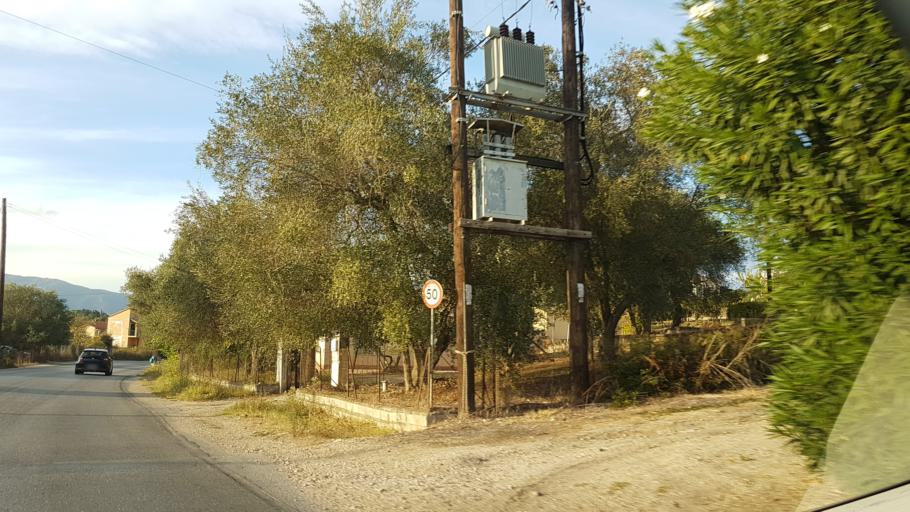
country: GR
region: Ionian Islands
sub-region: Nomos Kerkyras
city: Kontokali
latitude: 39.6653
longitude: 19.8437
